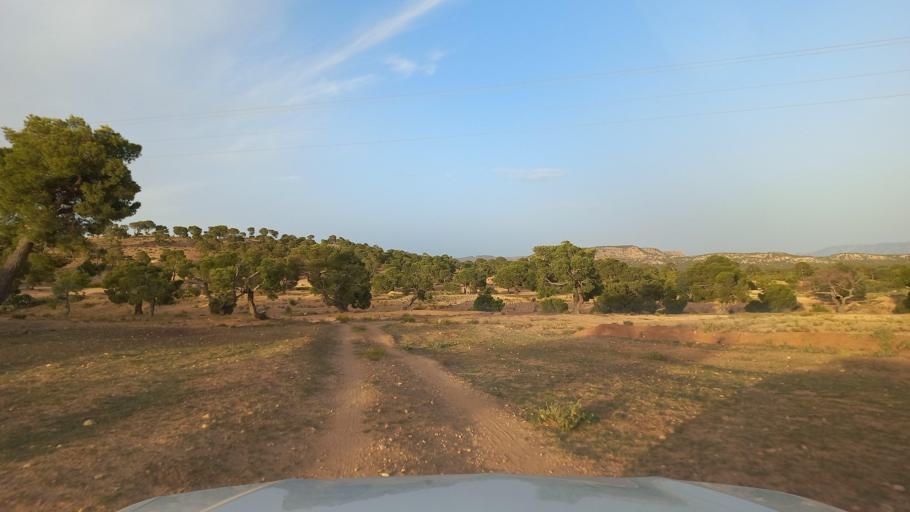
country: TN
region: Al Qasrayn
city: Sbiba
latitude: 35.4141
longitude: 8.9093
